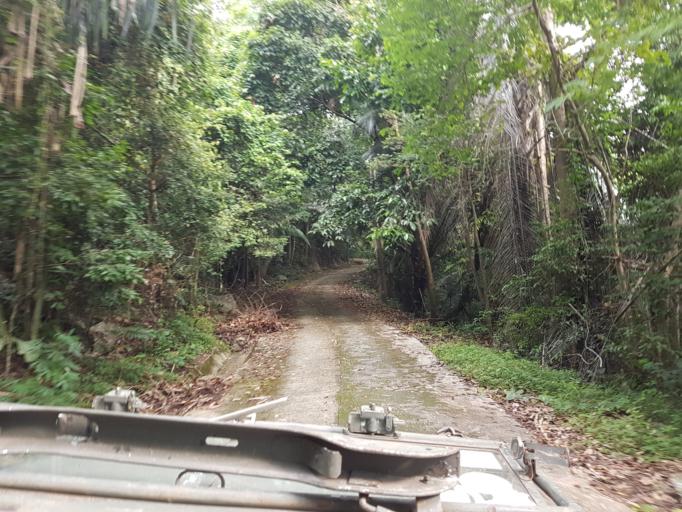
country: TH
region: Pattani
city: Khok Pho
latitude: 6.6565
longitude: 101.0987
